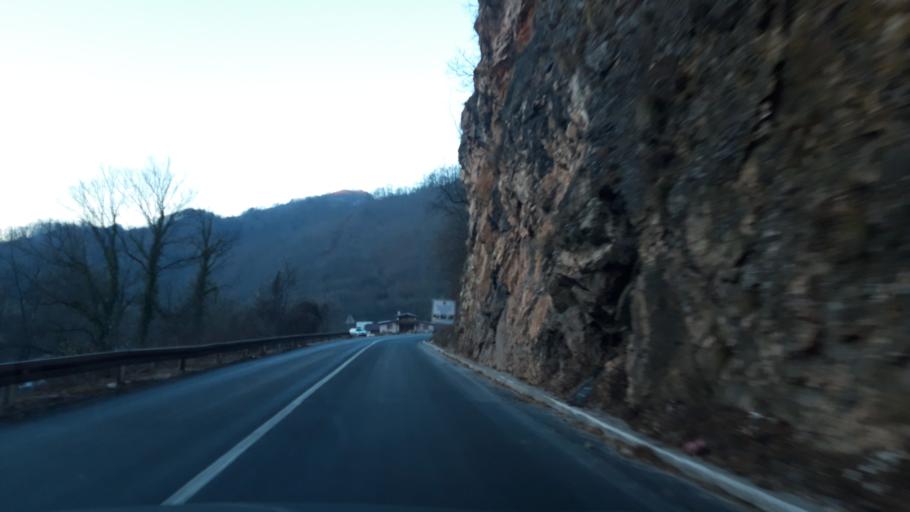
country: RS
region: Central Serbia
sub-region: Macvanski Okrug
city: Mali Zvornik
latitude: 44.2765
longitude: 19.1092
